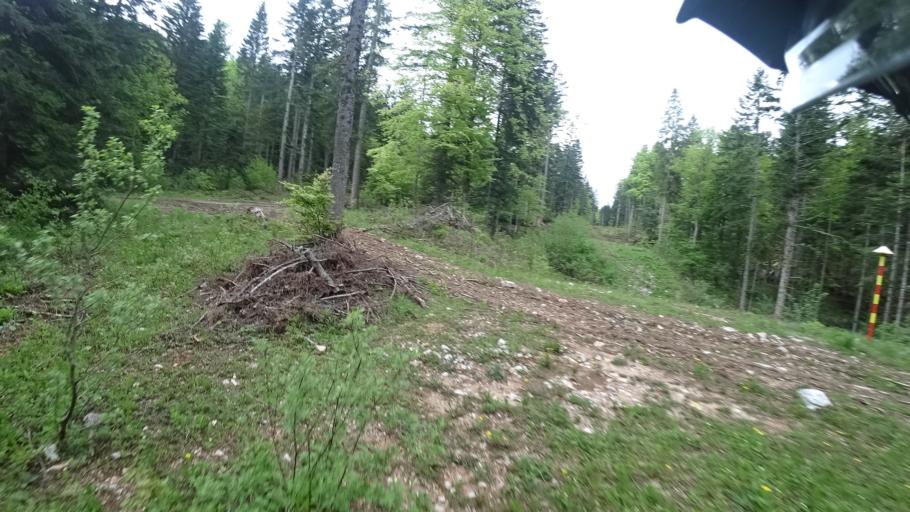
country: HR
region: Karlovacka
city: Plaski
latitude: 44.9529
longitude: 15.4149
